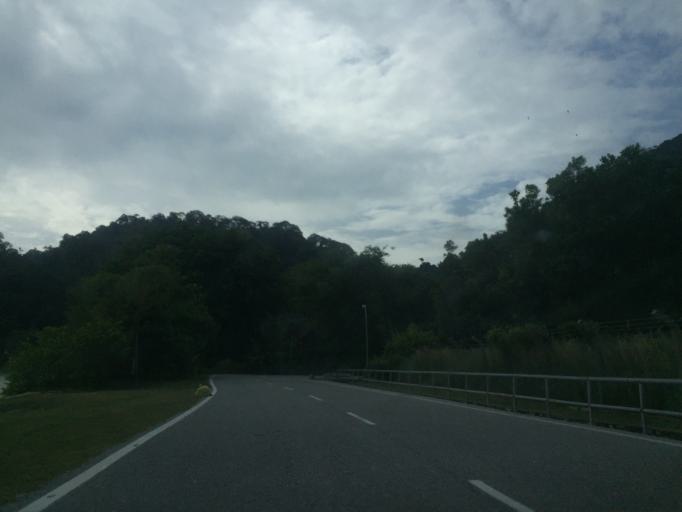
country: MY
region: Perak
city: Lumut
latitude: 4.2481
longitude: 100.5560
